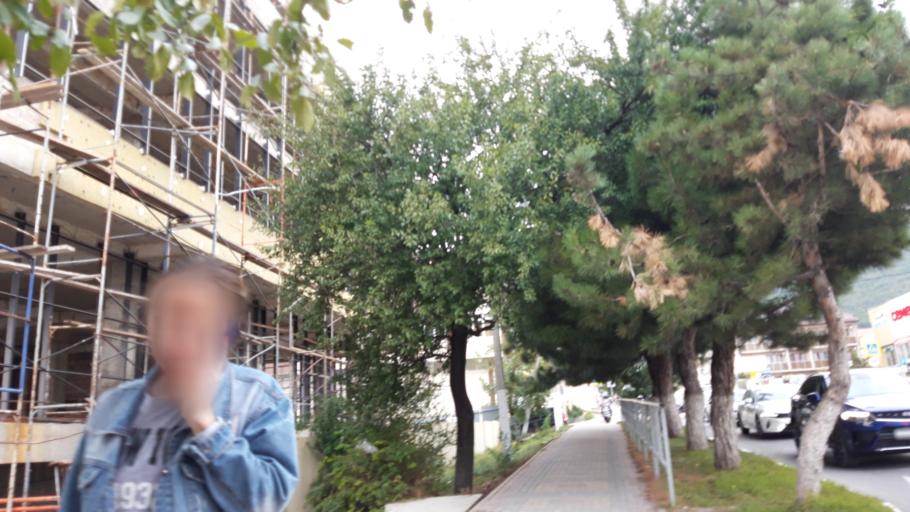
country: RU
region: Krasnodarskiy
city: Gelendzhik
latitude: 44.5675
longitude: 38.0890
